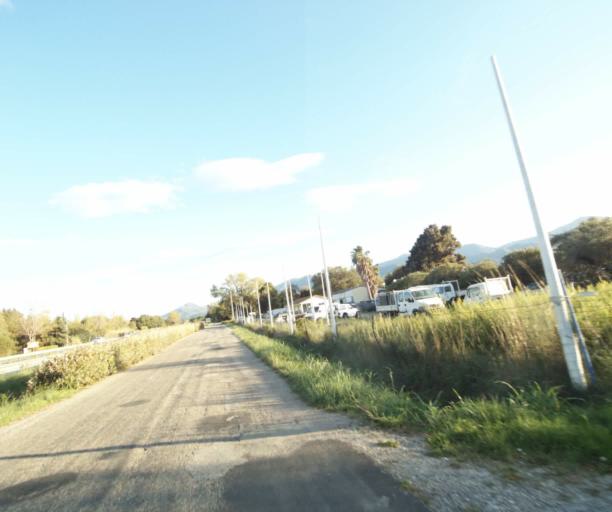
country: FR
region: Languedoc-Roussillon
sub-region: Departement des Pyrenees-Orientales
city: Sant Andreu de Sureda
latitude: 42.5740
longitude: 2.9957
